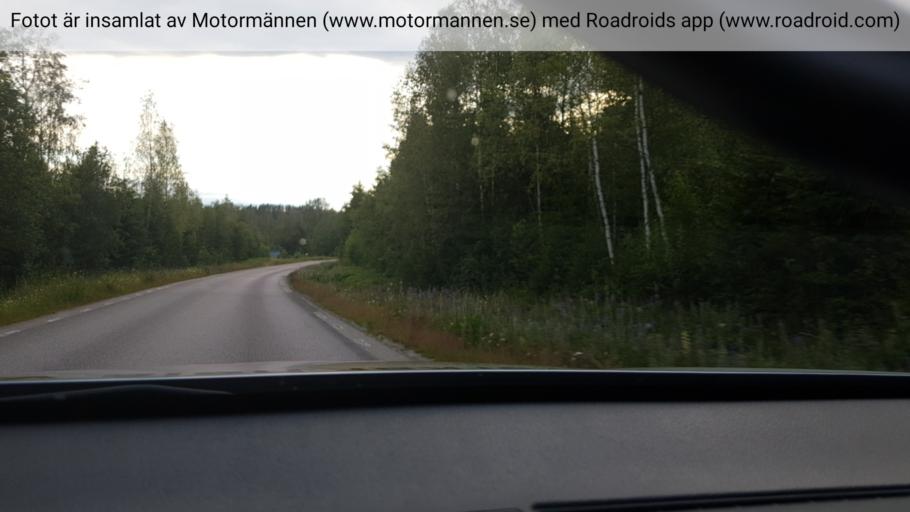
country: SE
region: Vaermland
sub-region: Forshaga Kommun
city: Deje
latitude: 59.7442
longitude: 13.3472
